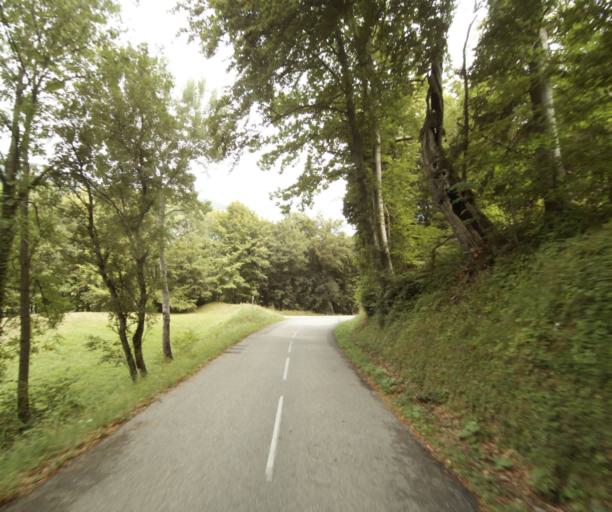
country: FR
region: Rhone-Alpes
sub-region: Departement de l'Isere
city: Saint-Egreve
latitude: 45.2668
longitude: 5.7083
